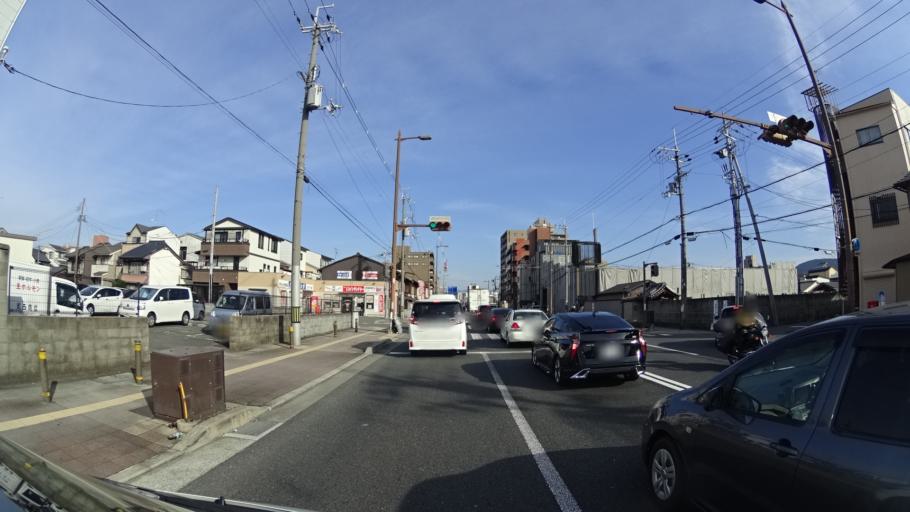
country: JP
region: Kyoto
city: Kyoto
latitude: 34.9777
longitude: 135.7640
